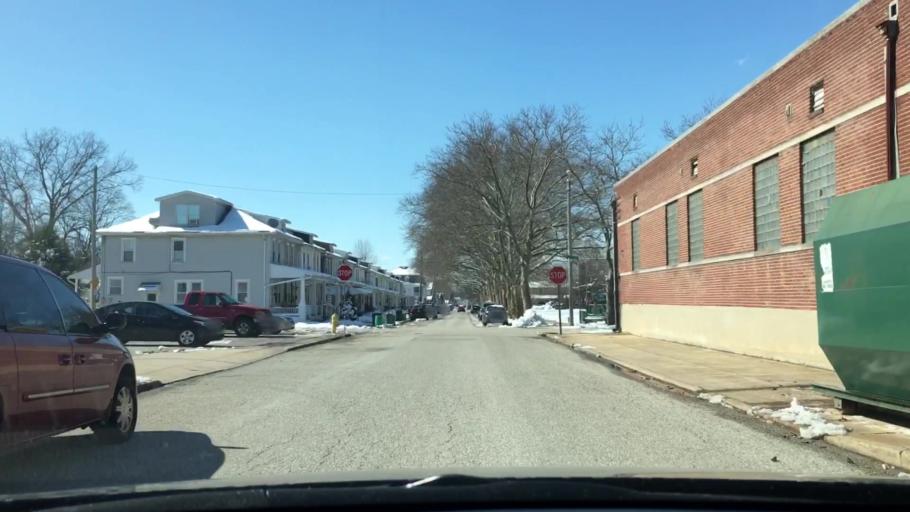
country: US
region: Pennsylvania
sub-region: York County
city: East York
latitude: 39.9683
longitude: -76.7035
